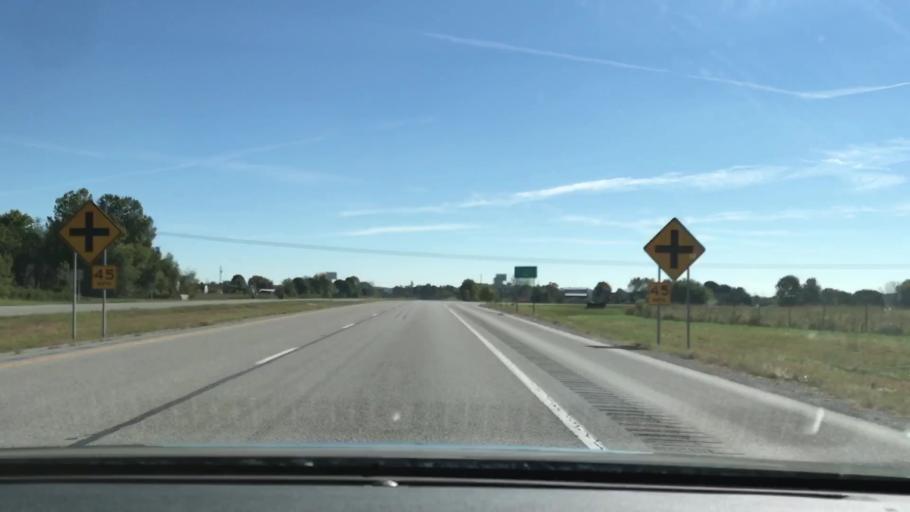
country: US
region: Kentucky
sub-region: Todd County
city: Elkton
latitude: 36.8230
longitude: -87.2010
